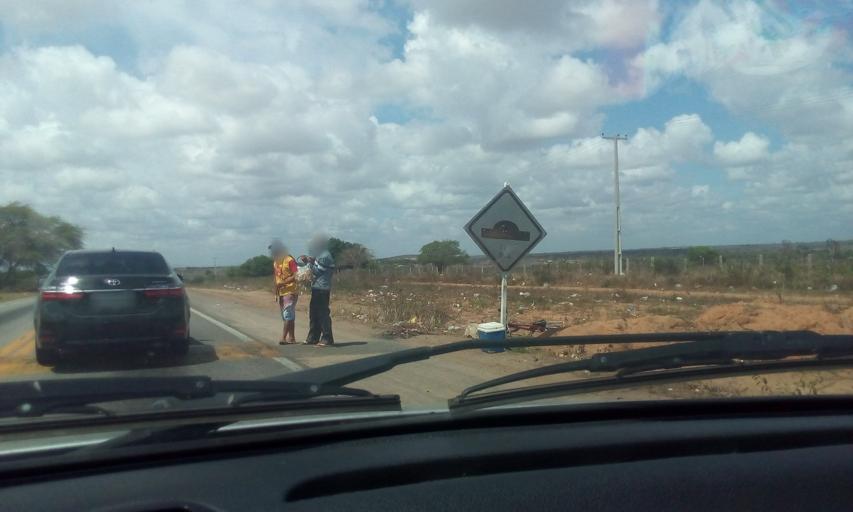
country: BR
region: Rio Grande do Norte
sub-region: Sao Paulo Do Potengi
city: Sao Paulo do Potengi
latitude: -5.9885
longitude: -35.5913
